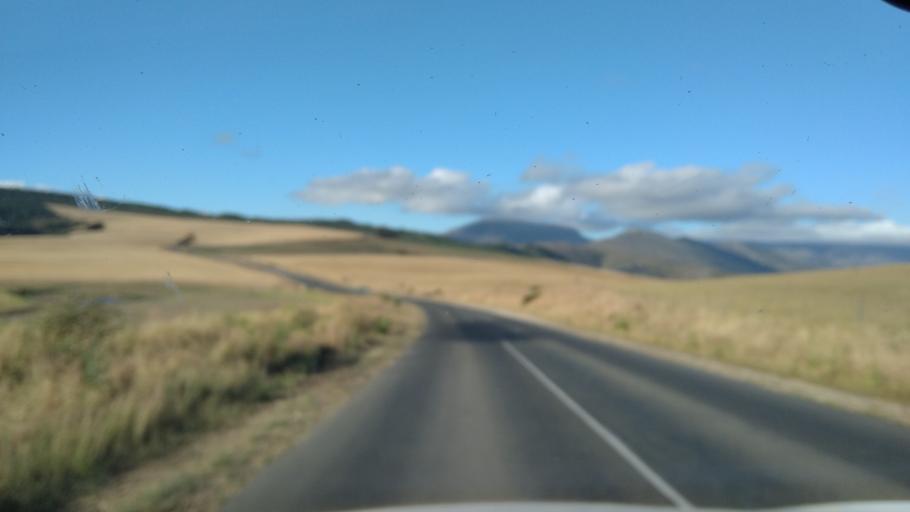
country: ZA
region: Western Cape
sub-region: Overberg District Municipality
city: Caledon
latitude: -34.1231
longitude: 19.2994
